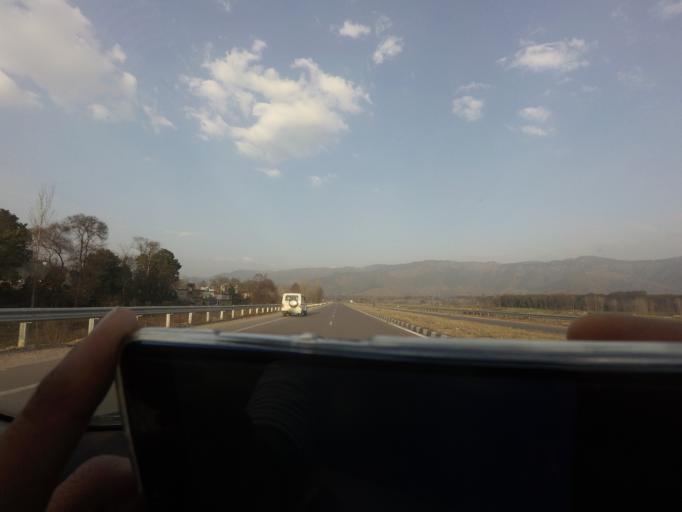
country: IN
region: Himachal Pradesh
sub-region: Mandi
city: Sundarnagar
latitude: 31.6110
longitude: 76.9320
